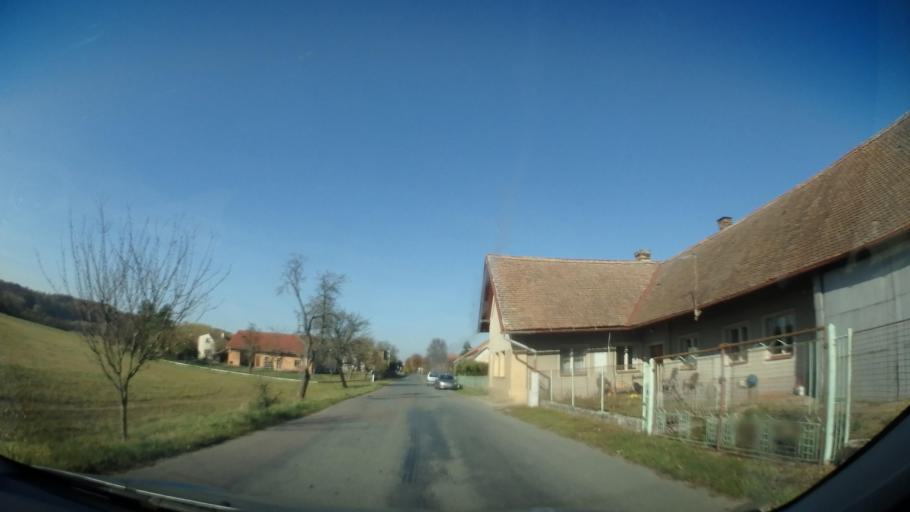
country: CZ
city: Ceske Mezirici
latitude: 50.2338
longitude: 16.0392
